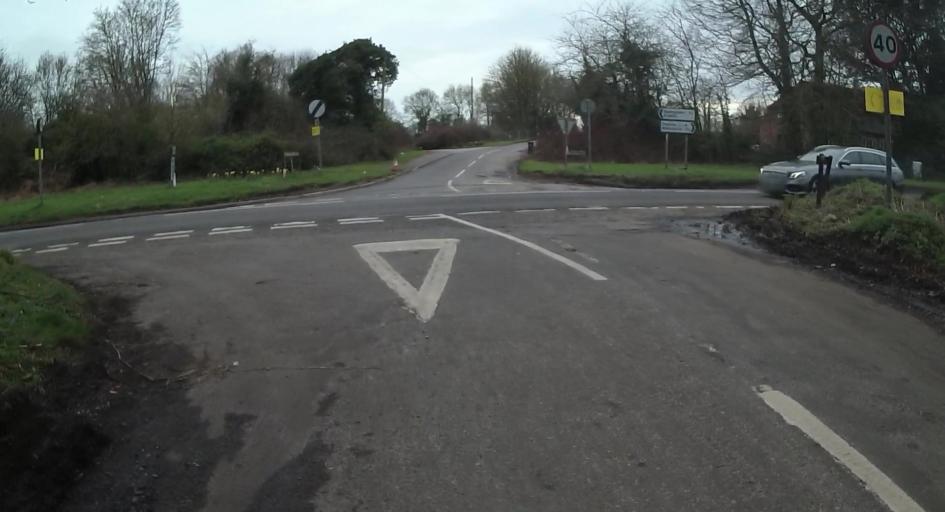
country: GB
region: England
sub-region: Hampshire
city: Overton
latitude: 51.2559
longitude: -1.1841
